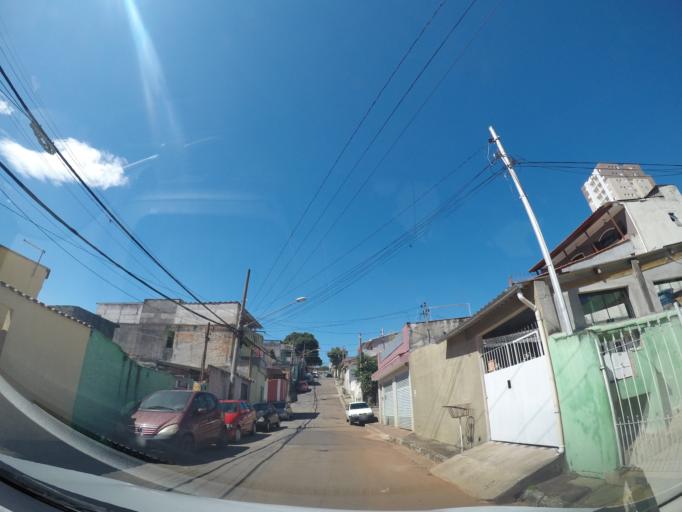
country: BR
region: Sao Paulo
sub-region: Guarulhos
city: Guarulhos
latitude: -23.4530
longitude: -46.5444
